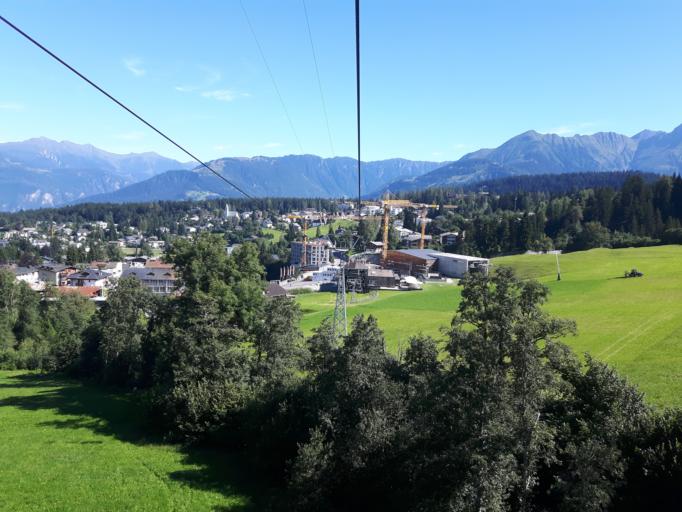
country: CH
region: Grisons
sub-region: Imboden District
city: Flims
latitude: 46.8358
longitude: 9.2794
